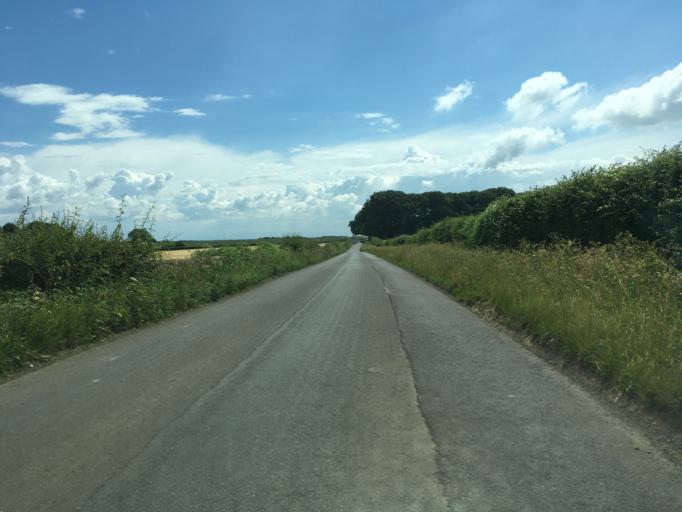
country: GB
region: England
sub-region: Gloucestershire
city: Coates
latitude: 51.7176
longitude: -2.0879
